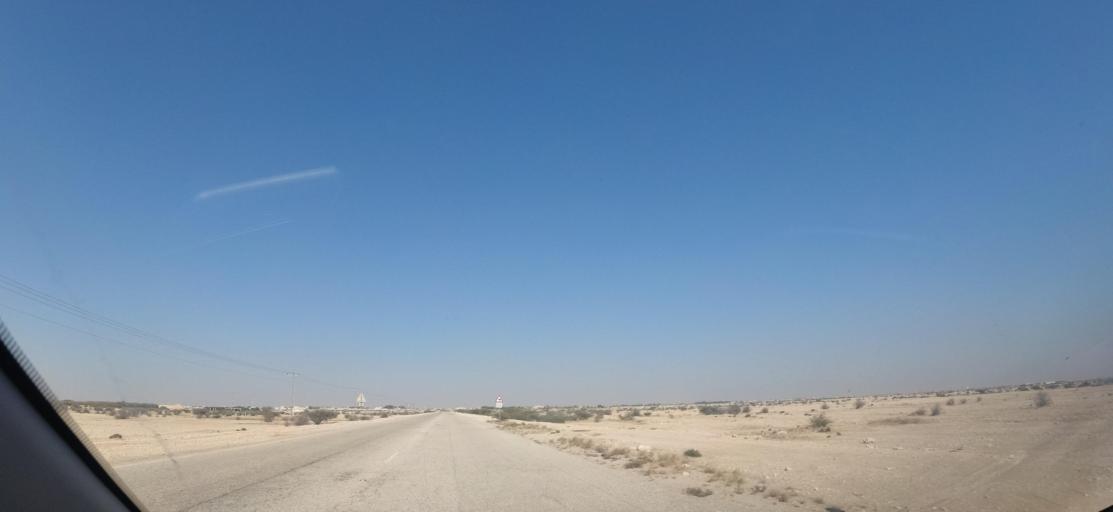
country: QA
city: Al Jumayliyah
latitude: 25.6012
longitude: 51.0723
